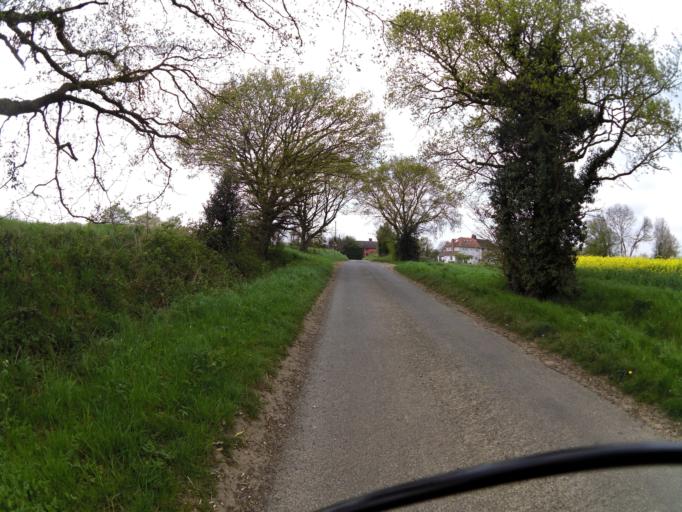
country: GB
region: England
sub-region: Suffolk
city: Hadleigh
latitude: 52.0503
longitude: 0.8954
